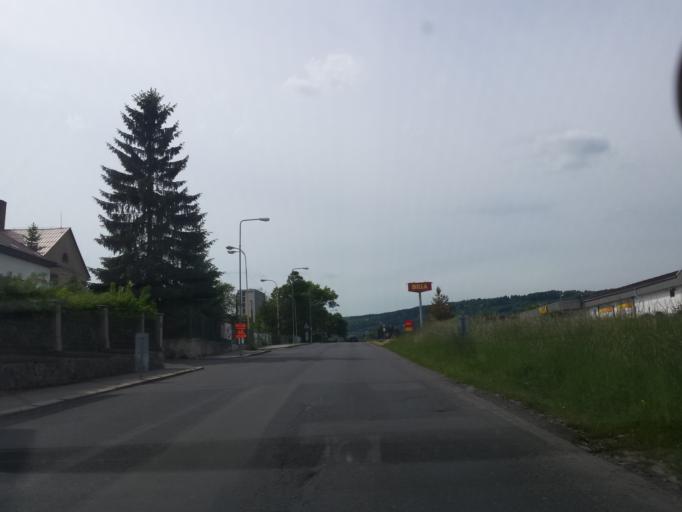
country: CZ
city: Novy Bor
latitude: 50.7635
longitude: 14.5479
